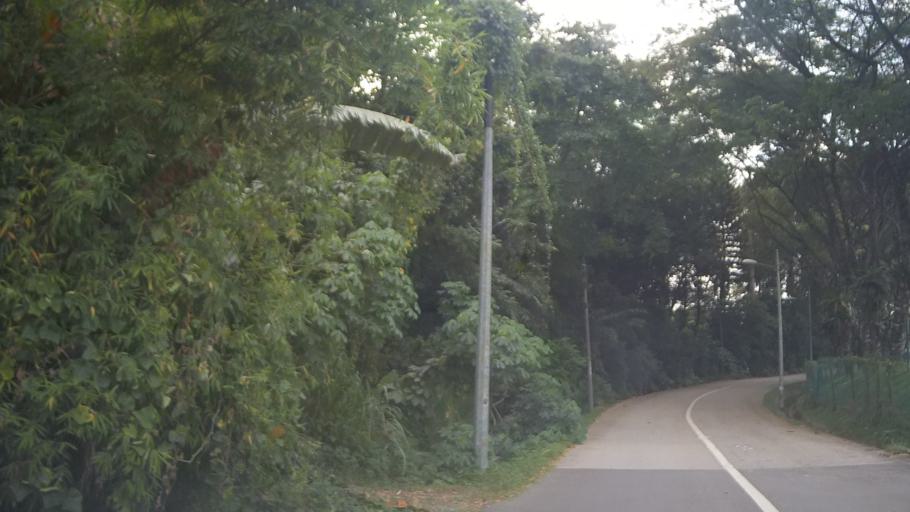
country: MY
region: Johor
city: Kampung Pasir Gudang Baru
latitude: 1.3973
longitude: 103.8672
